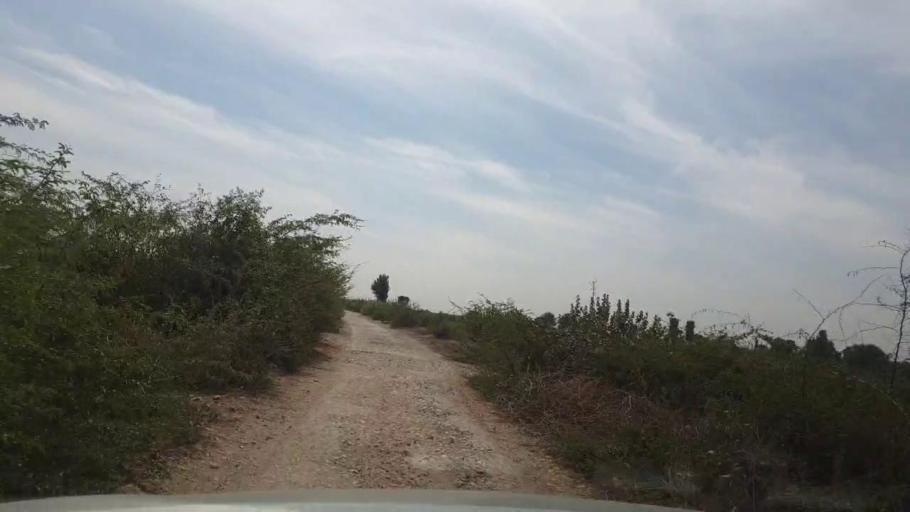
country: PK
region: Sindh
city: Nabisar
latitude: 25.0745
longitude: 69.5987
